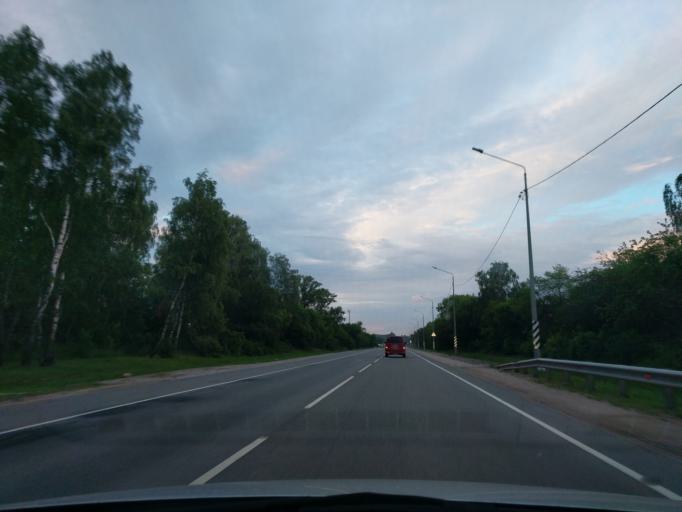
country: RU
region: Kaluga
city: Obninsk
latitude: 55.0663
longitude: 36.6006
